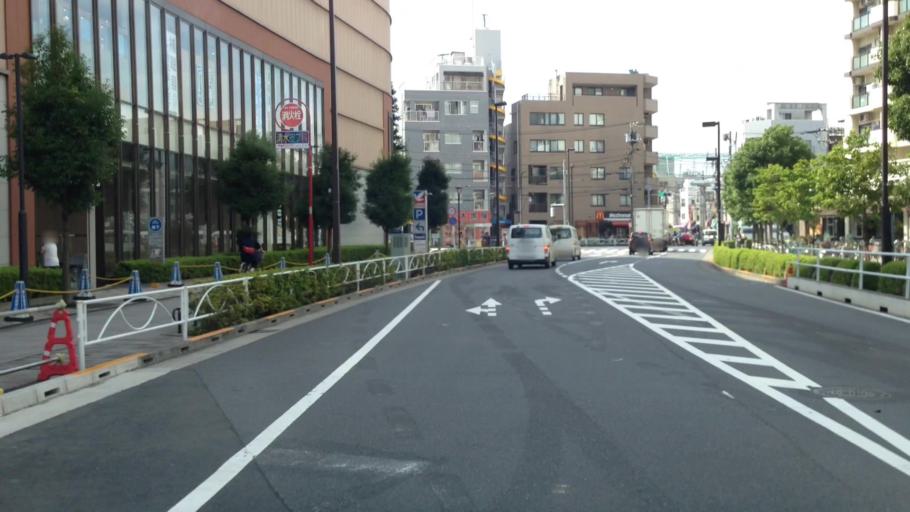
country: JP
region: Tokyo
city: Urayasu
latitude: 35.7174
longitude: 139.8185
